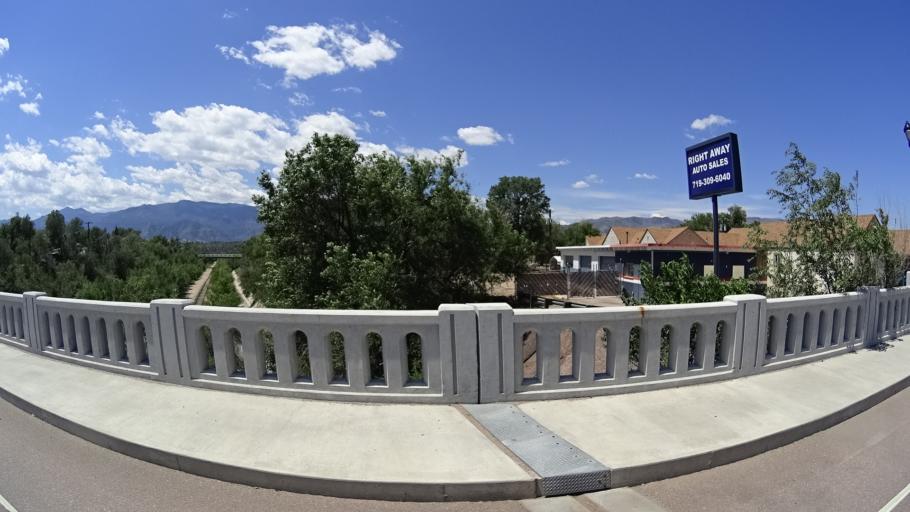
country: US
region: Colorado
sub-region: El Paso County
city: Colorado Springs
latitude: 38.8710
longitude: -104.8199
